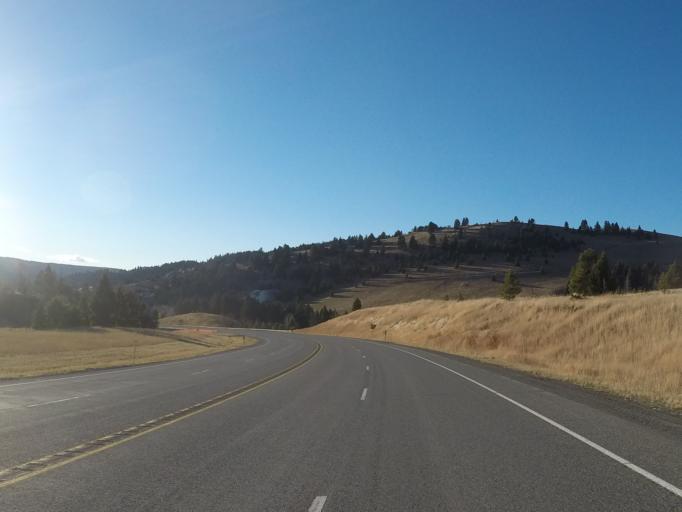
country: US
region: Montana
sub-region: Lewis and Clark County
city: Helena West Side
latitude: 46.5625
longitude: -112.3751
